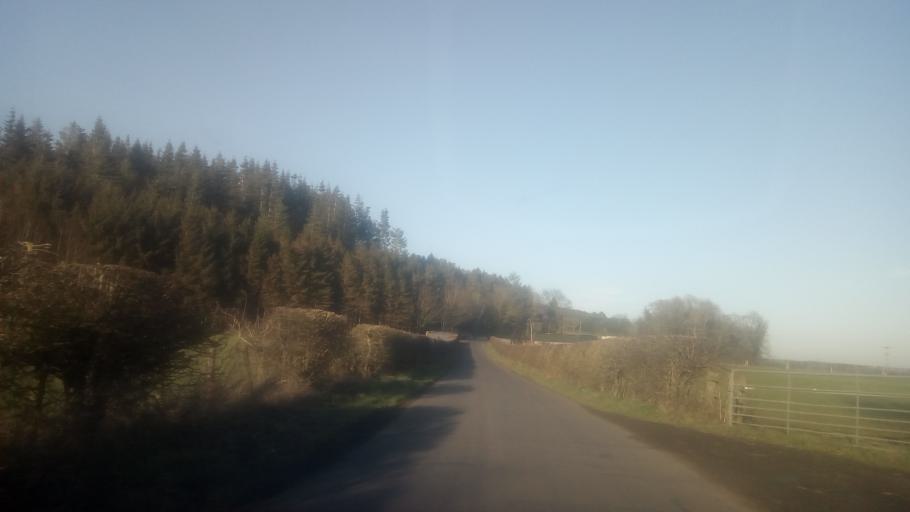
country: GB
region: Scotland
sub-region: The Scottish Borders
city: Saint Boswells
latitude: 55.4687
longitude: -2.6714
